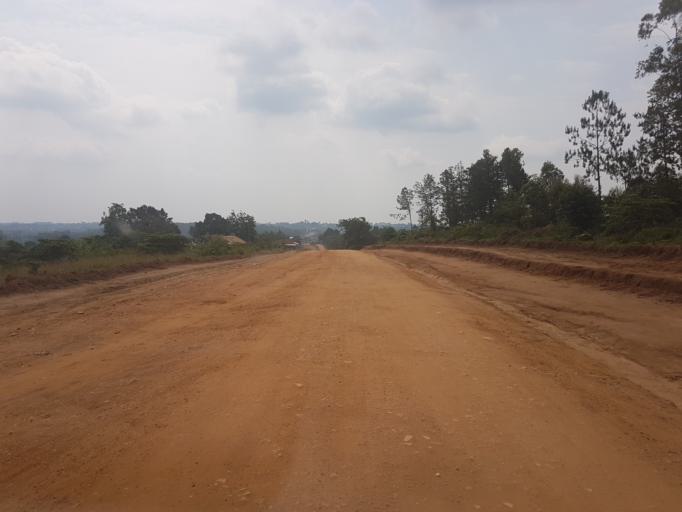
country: UG
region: Western Region
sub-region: Kanungu District
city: Ntungamo
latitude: -0.8102
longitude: 29.7059
